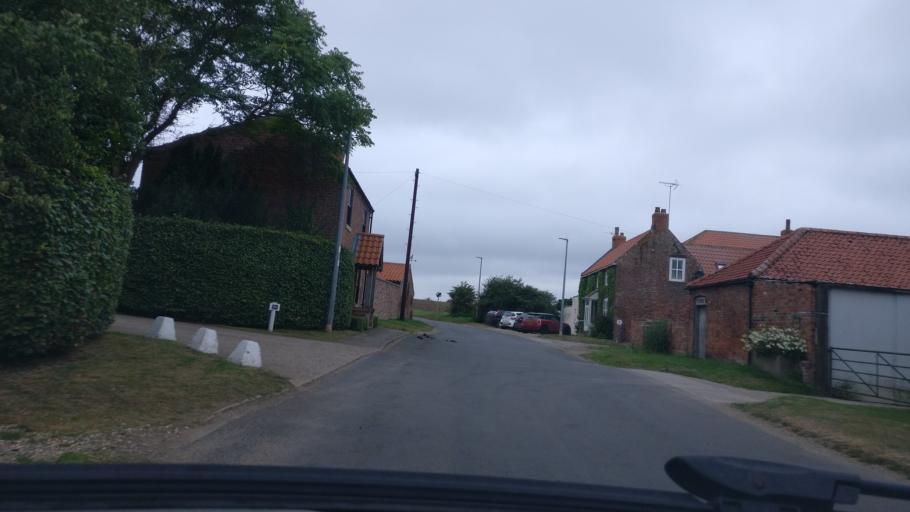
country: GB
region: England
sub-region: East Riding of Yorkshire
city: Leven
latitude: 53.8934
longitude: -0.3273
